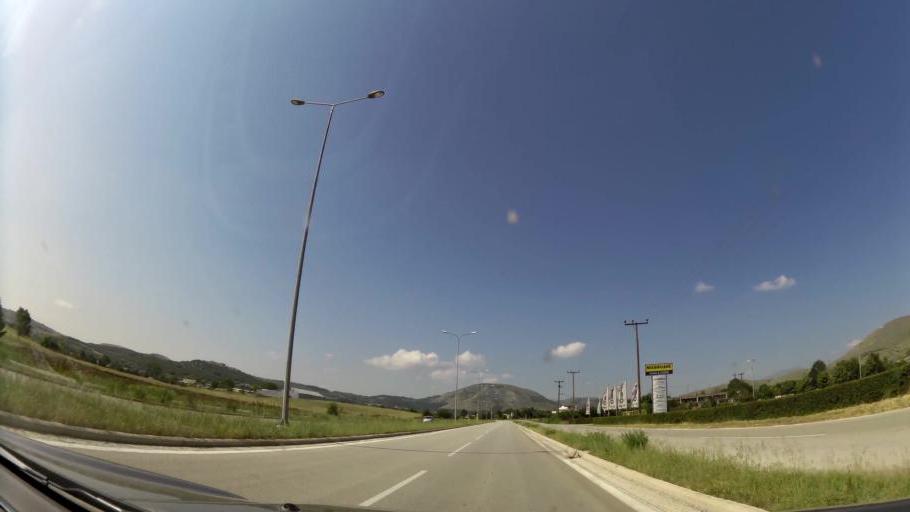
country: GR
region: West Macedonia
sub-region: Nomos Kozanis
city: Koila
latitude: 40.3425
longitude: 21.7957
